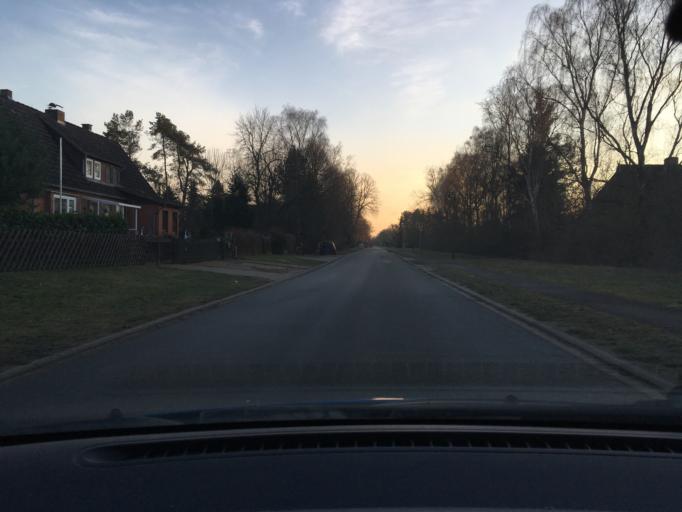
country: DE
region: Schleswig-Holstein
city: Langenlehsten
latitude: 53.5023
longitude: 10.7414
